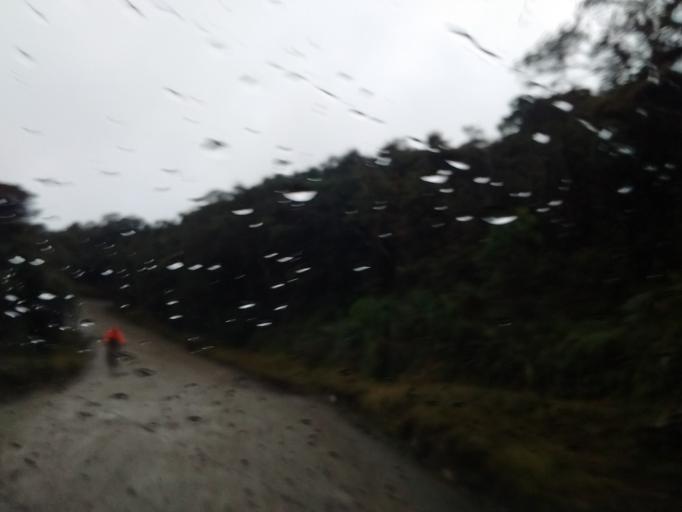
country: CO
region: Cauca
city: Paispamba
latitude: 2.1672
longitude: -76.4099
